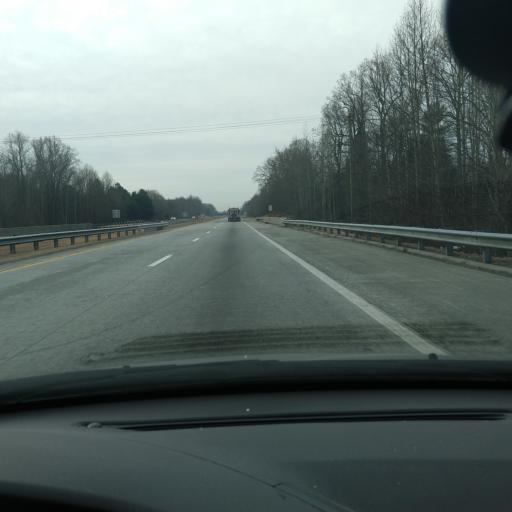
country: US
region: North Carolina
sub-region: Davidson County
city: Lexington
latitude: 35.8285
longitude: -80.2837
